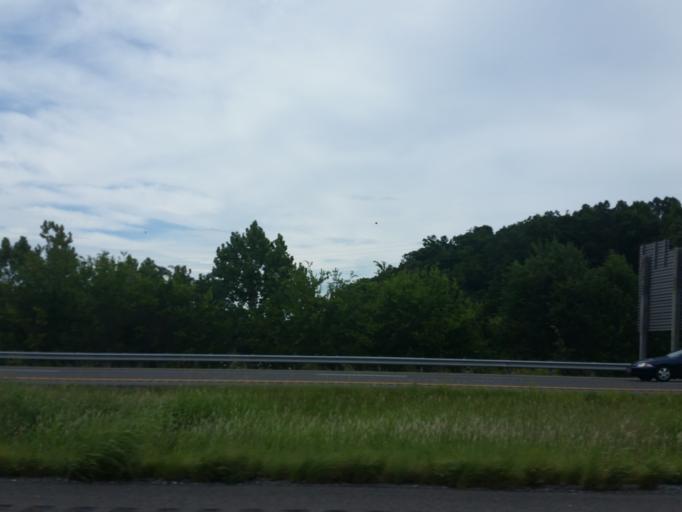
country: US
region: Kentucky
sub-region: Lyon County
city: Eddyville
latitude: 37.0718
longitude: -88.0972
